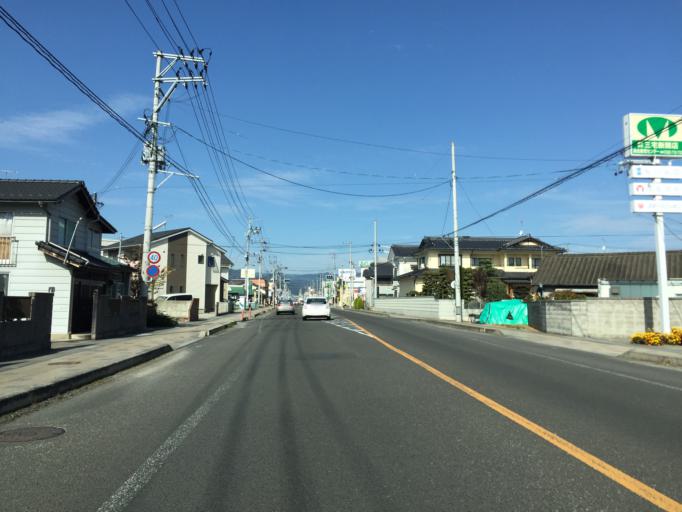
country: JP
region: Fukushima
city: Fukushima-shi
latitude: 37.7699
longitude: 140.4526
